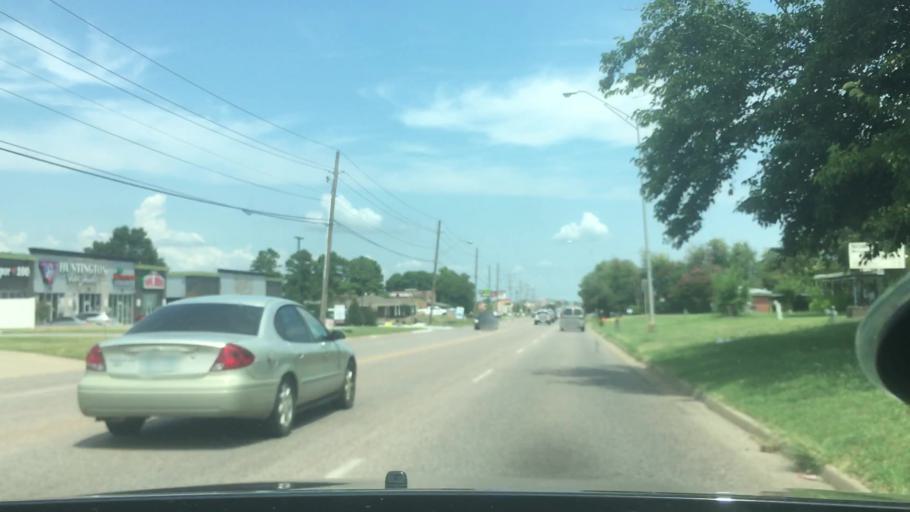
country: US
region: Oklahoma
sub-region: Pottawatomie County
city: Shawnee
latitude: 35.3724
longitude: -96.9297
